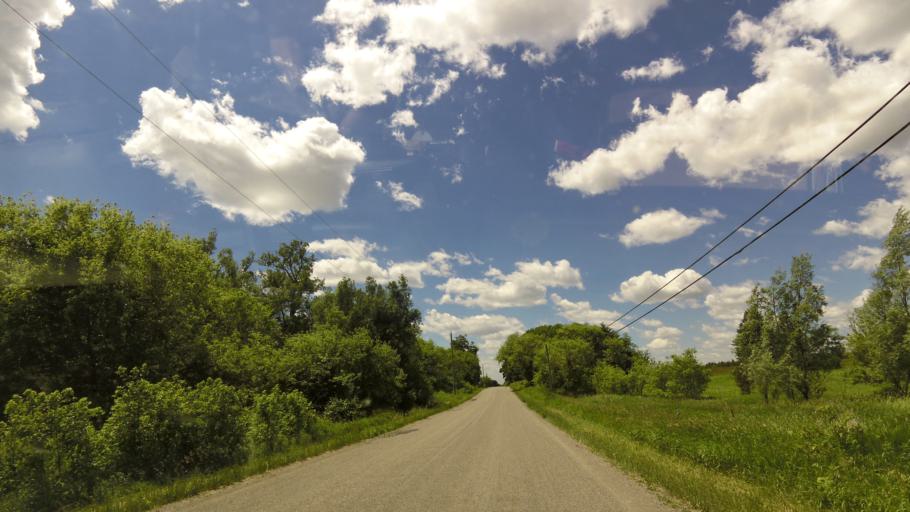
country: CA
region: Ontario
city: Oshawa
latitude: 43.9738
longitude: -78.6005
